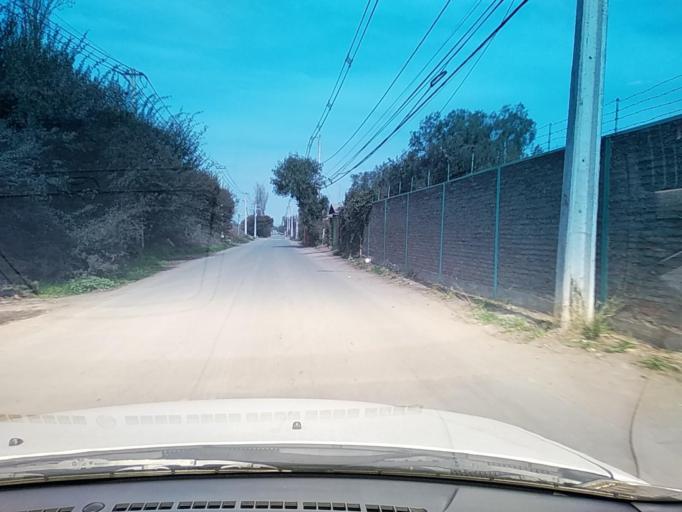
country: CL
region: Santiago Metropolitan
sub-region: Provincia de Chacabuco
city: Chicureo Abajo
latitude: -33.2975
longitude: -70.7225
